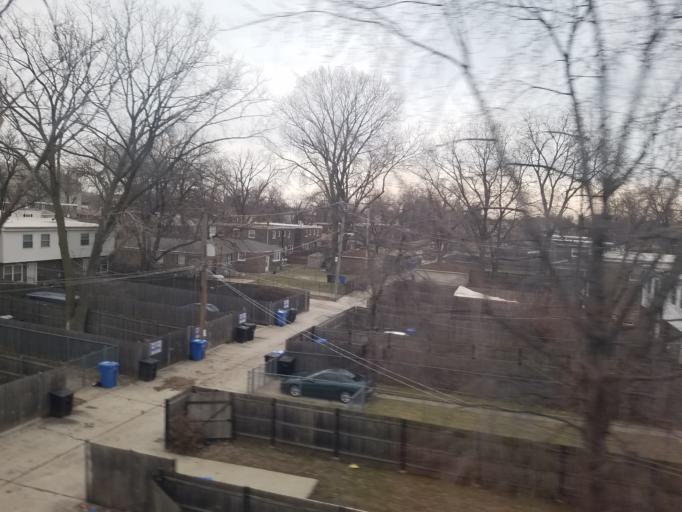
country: US
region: Illinois
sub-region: Cook County
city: Chicago
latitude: 41.8169
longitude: -87.6356
